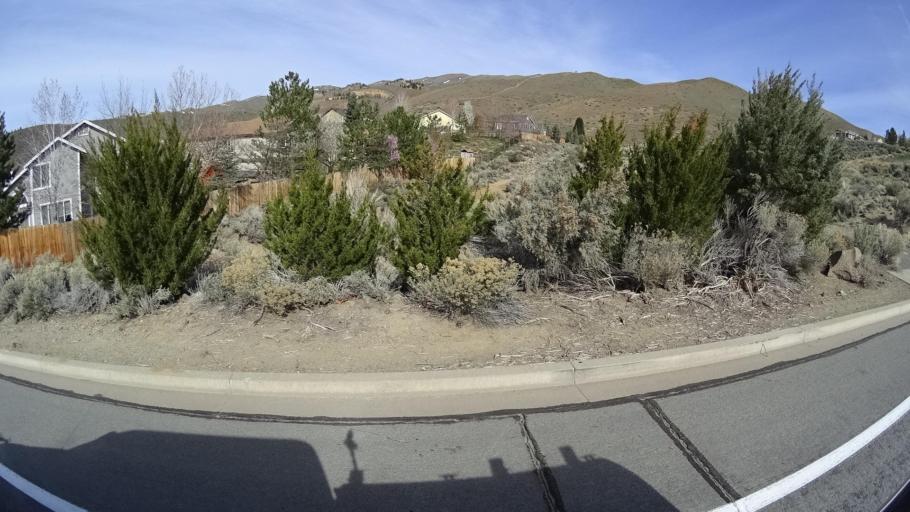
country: US
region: Nevada
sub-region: Washoe County
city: Mogul
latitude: 39.5467
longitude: -119.8986
